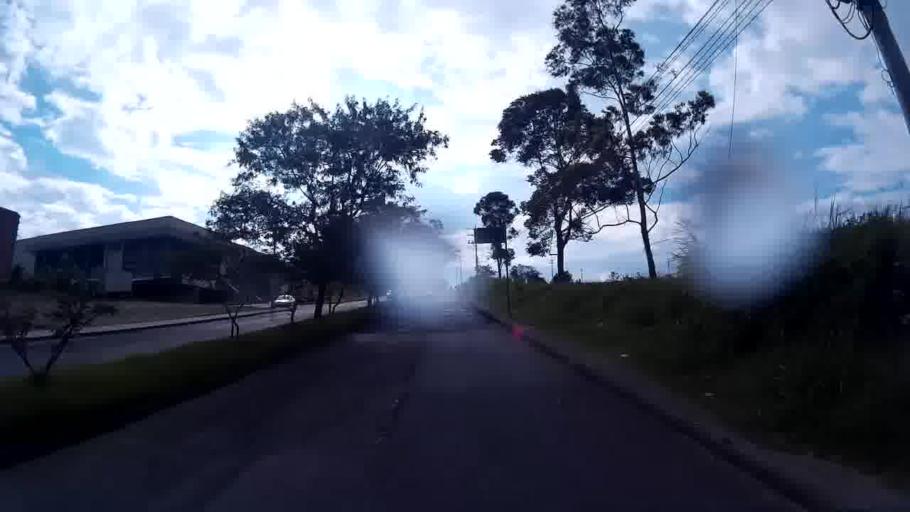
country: CO
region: Quindio
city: Calarca
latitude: 4.5612
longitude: -75.6501
